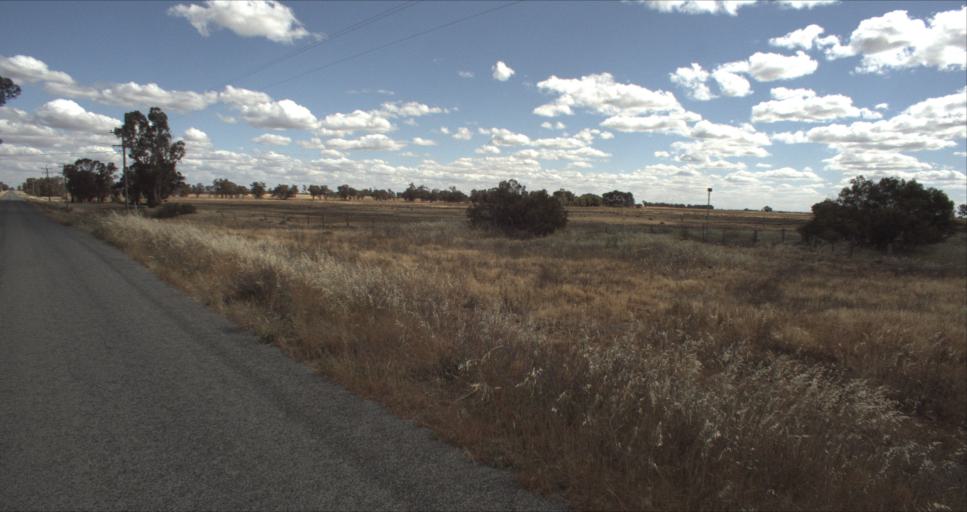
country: AU
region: New South Wales
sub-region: Leeton
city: Leeton
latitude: -34.4840
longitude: 146.2485
